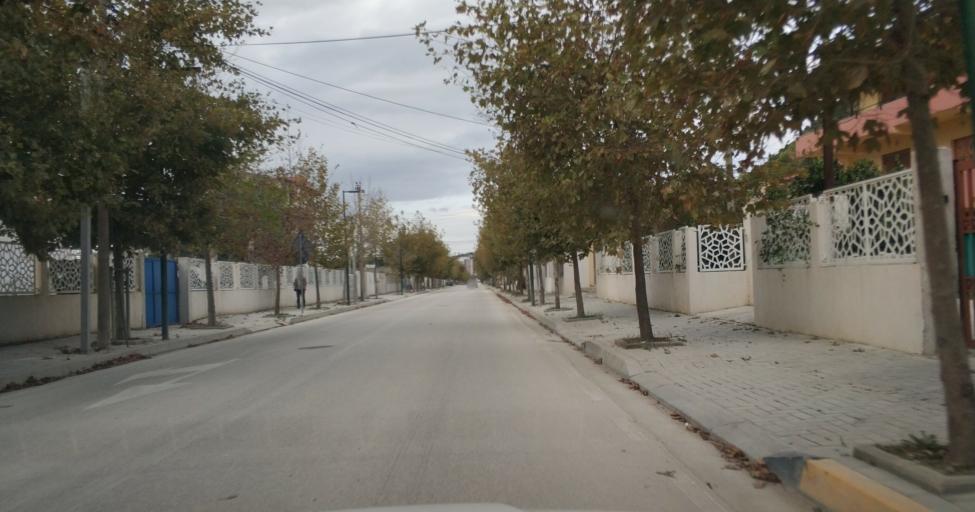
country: AL
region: Vlore
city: Vlore
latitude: 40.4472
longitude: 19.4967
